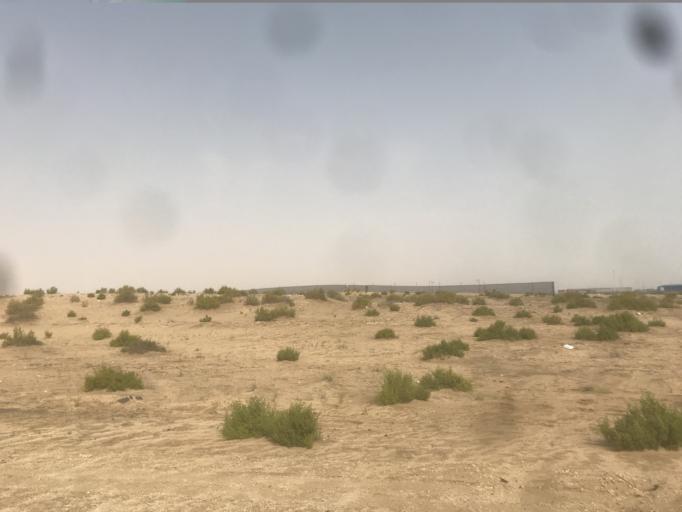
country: SA
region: Eastern Province
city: Abqaiq
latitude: 25.9106
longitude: 49.9514
